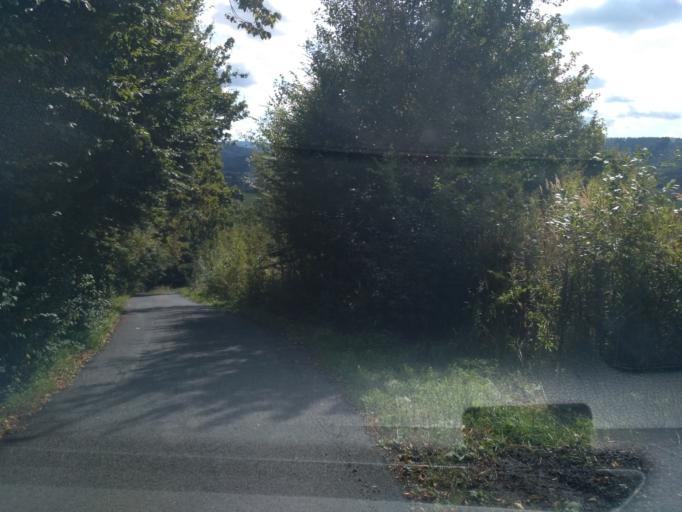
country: PL
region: Subcarpathian Voivodeship
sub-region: Powiat strzyzowski
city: Strzyzow
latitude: 49.8479
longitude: 21.8246
